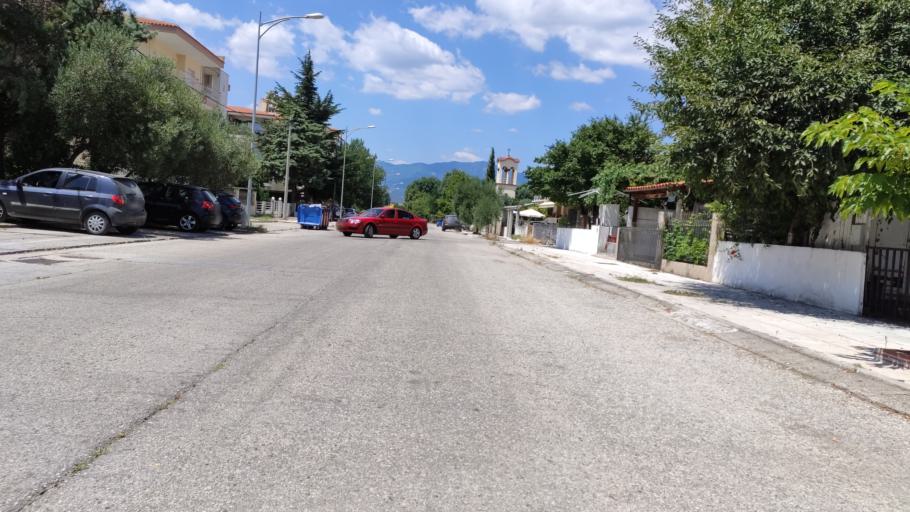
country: GR
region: East Macedonia and Thrace
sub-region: Nomos Rodopis
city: Komotini
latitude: 41.1253
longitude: 25.3993
